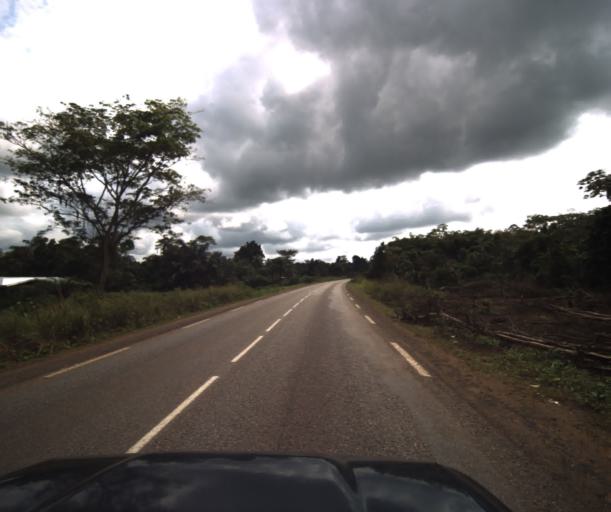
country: CM
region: Littoral
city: Edea
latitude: 3.8120
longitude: 10.3032
